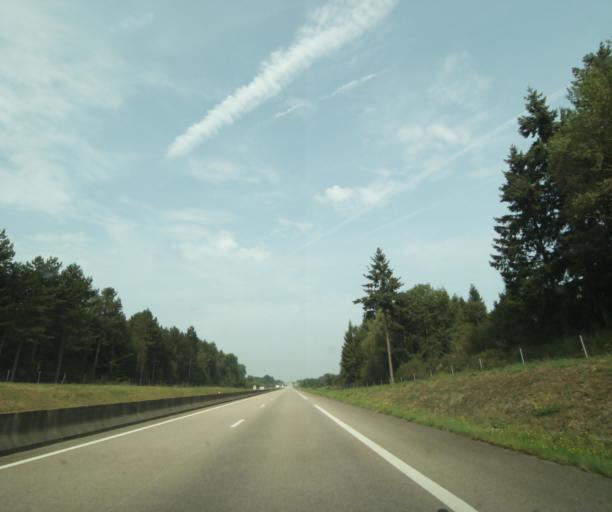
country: FR
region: Lower Normandy
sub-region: Departement du Calvados
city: Falaise
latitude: 48.8345
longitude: -0.1514
